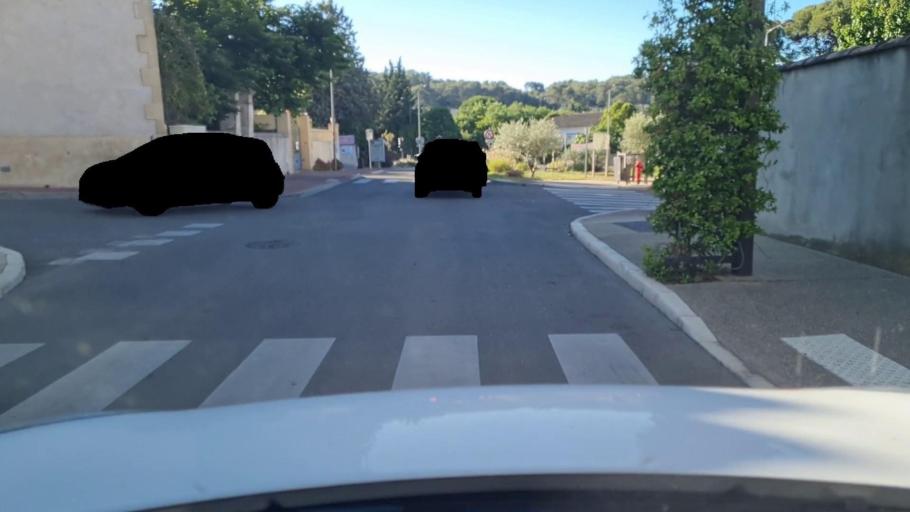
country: FR
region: Languedoc-Roussillon
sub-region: Departement du Gard
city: Caveirac
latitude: 43.8229
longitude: 4.2645
